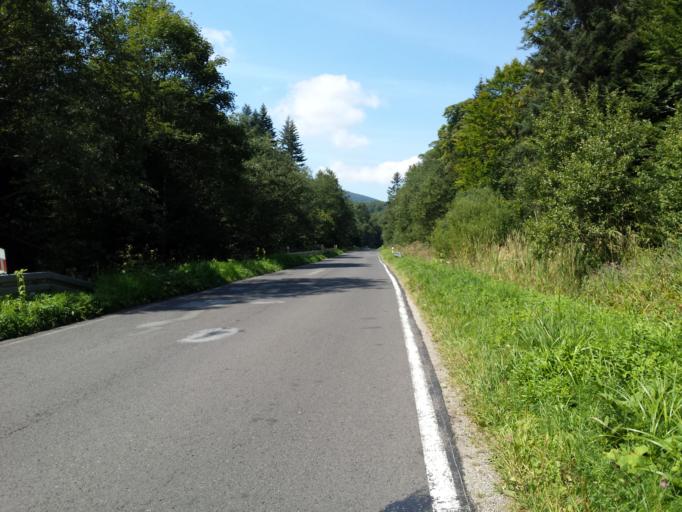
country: PL
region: Subcarpathian Voivodeship
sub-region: Powiat bieszczadzki
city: Lutowiska
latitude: 49.1122
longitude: 22.6176
